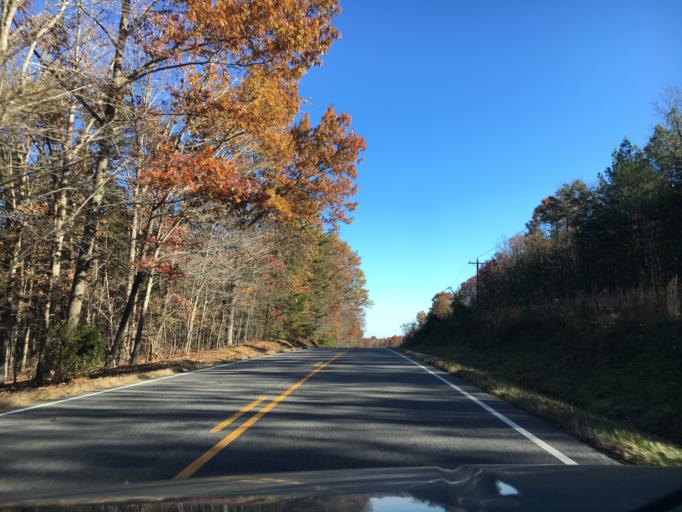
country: US
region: Virginia
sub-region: Buckingham County
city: Buckingham
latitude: 37.4657
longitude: -78.6668
